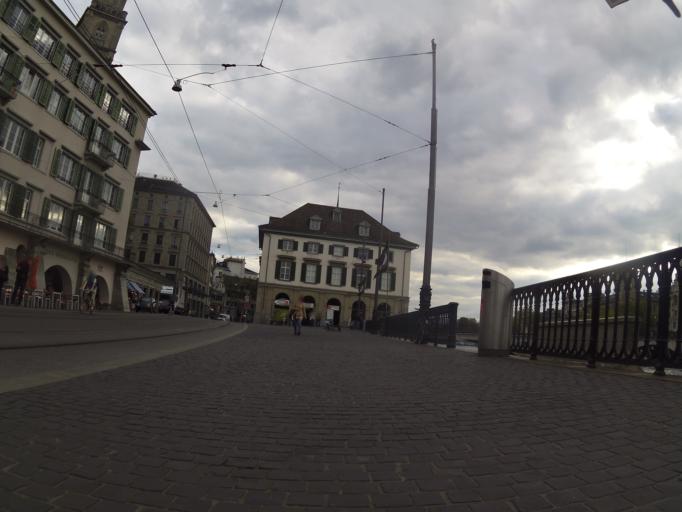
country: CH
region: Zurich
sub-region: Bezirk Zuerich
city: Zuerich (Kreis 1)
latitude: 47.3707
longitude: 8.5430
